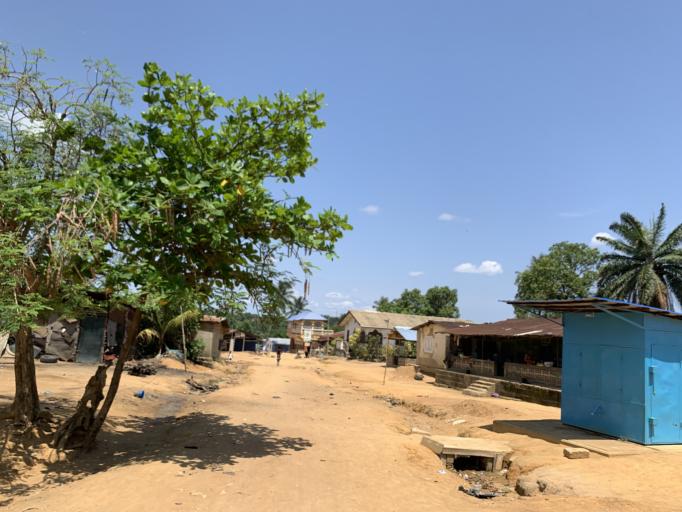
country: SL
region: Western Area
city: Waterloo
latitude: 8.3232
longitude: -13.0618
